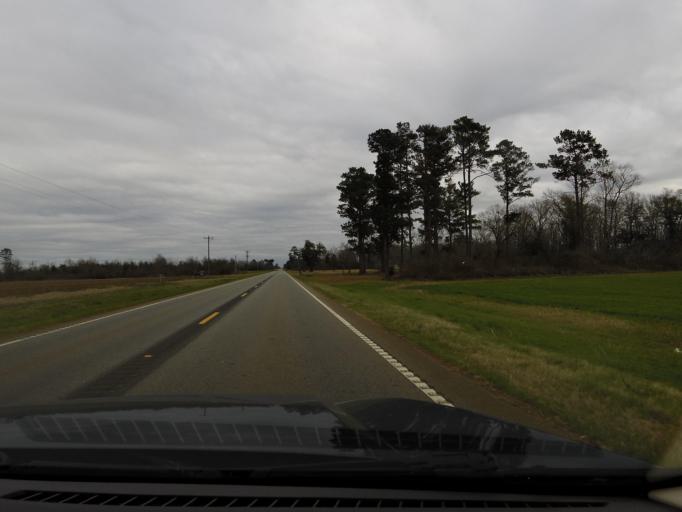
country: US
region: Georgia
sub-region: Randolph County
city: Shellman
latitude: 31.7727
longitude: -84.6638
